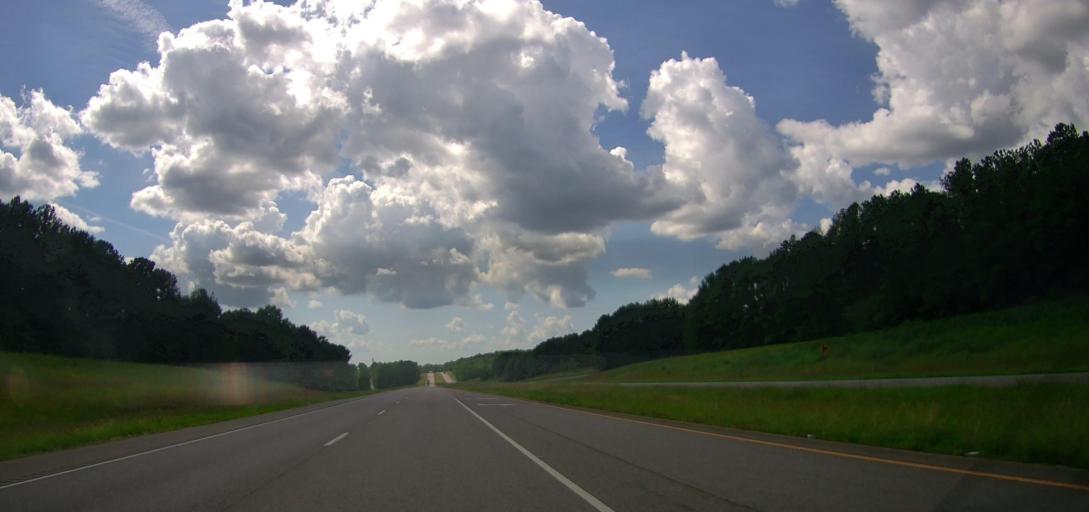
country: US
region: Alabama
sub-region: Pickens County
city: Reform
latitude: 33.3978
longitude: -88.0605
